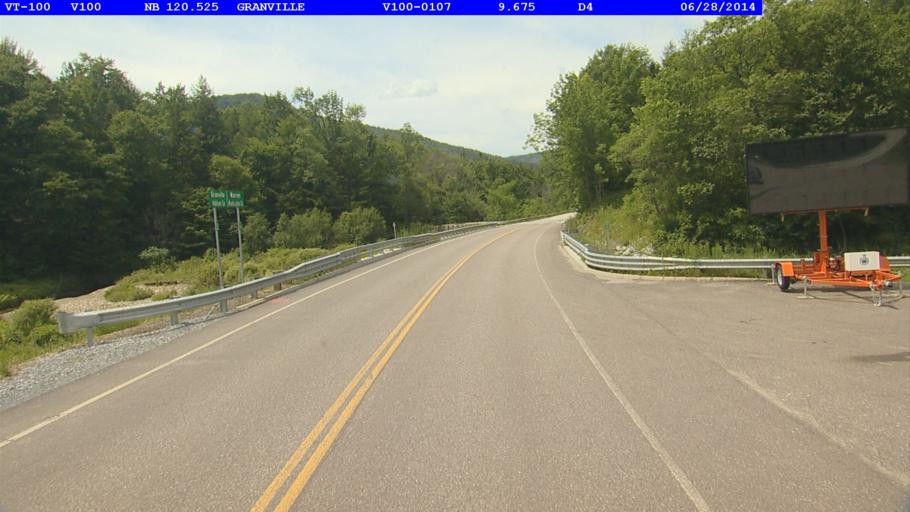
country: US
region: Vermont
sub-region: Washington County
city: Northfield
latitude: 44.0612
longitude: -72.8517
